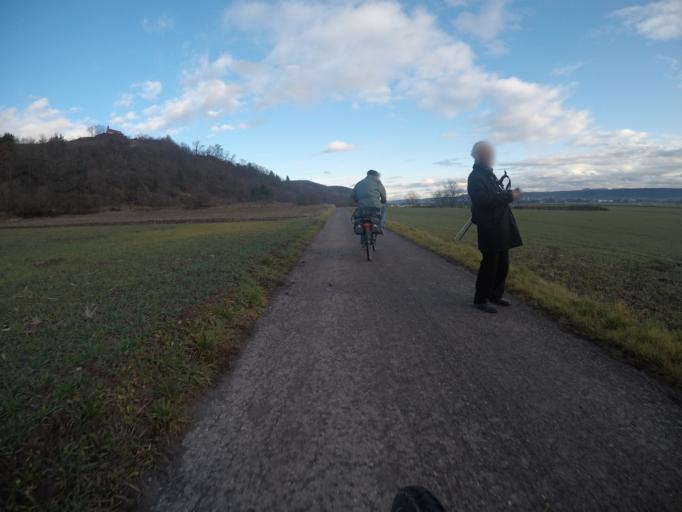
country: DE
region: Baden-Wuerttemberg
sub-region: Tuebingen Region
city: Rottenburg
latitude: 48.5030
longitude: 8.9781
